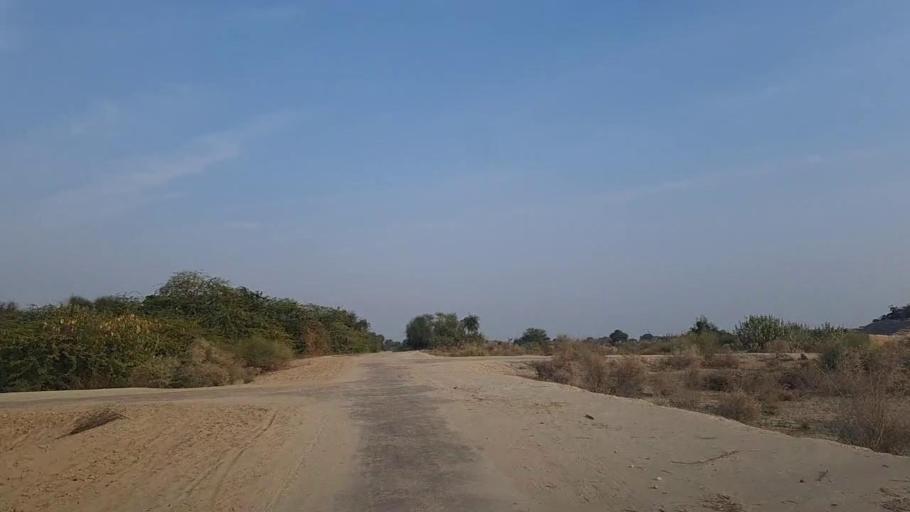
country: PK
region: Sindh
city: Jam Sahib
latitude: 26.4372
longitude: 68.5961
